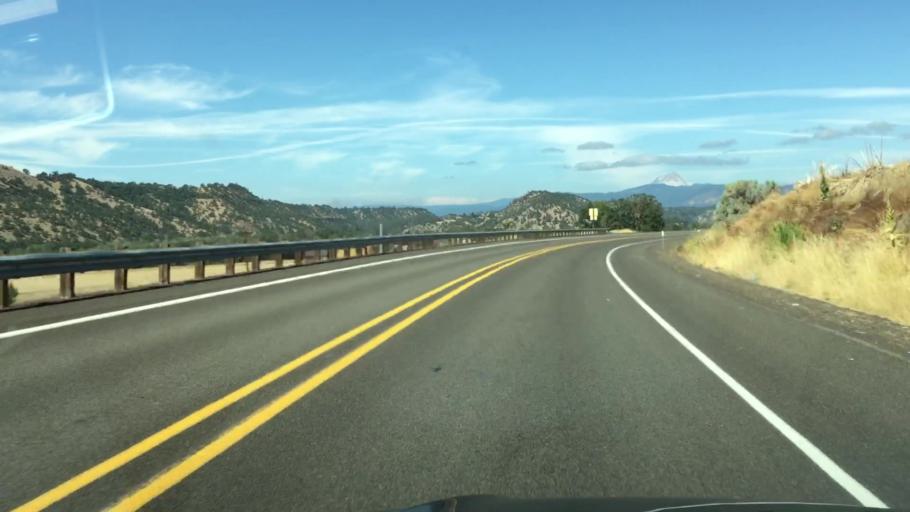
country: US
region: Oregon
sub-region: Wasco County
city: The Dalles
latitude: 45.2546
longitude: -121.1834
